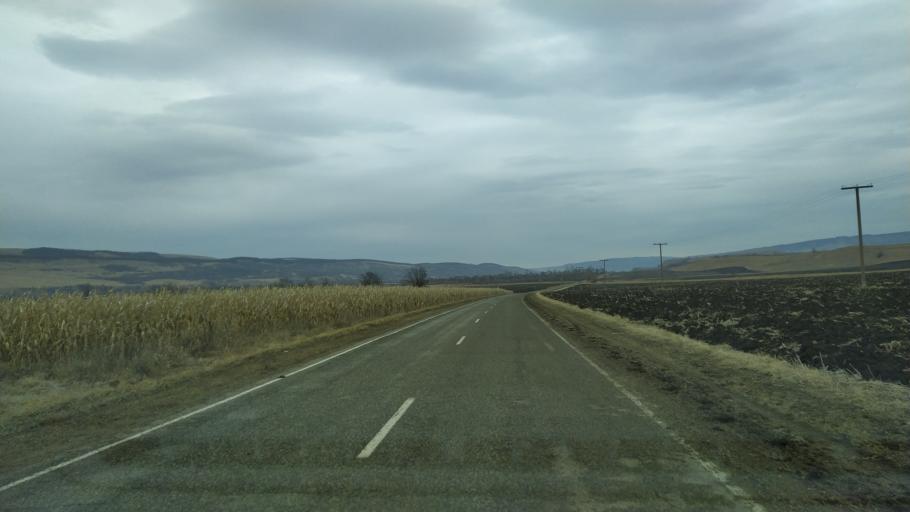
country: RU
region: Krasnodarskiy
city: Peredovaya
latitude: 44.0911
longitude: 41.3827
